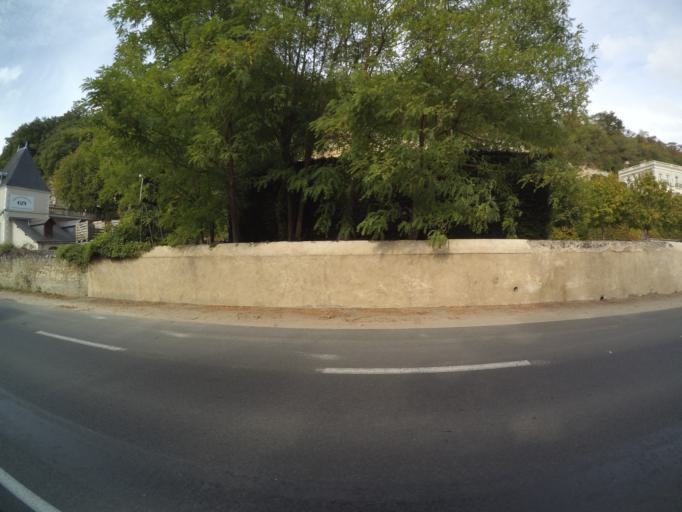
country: FR
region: Centre
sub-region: Departement d'Indre-et-Loire
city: La Ville-aux-Dames
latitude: 47.4102
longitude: 0.7736
